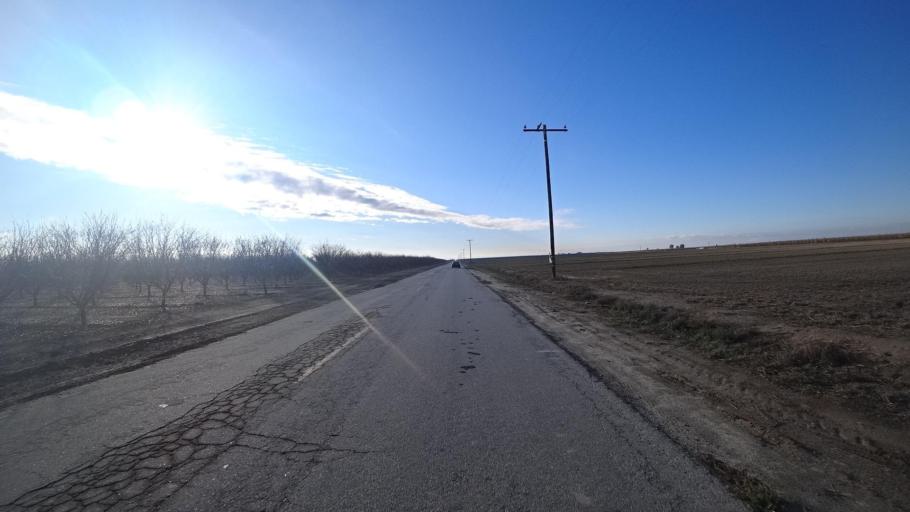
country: US
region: California
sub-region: Kern County
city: Delano
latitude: 35.7590
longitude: -119.3298
